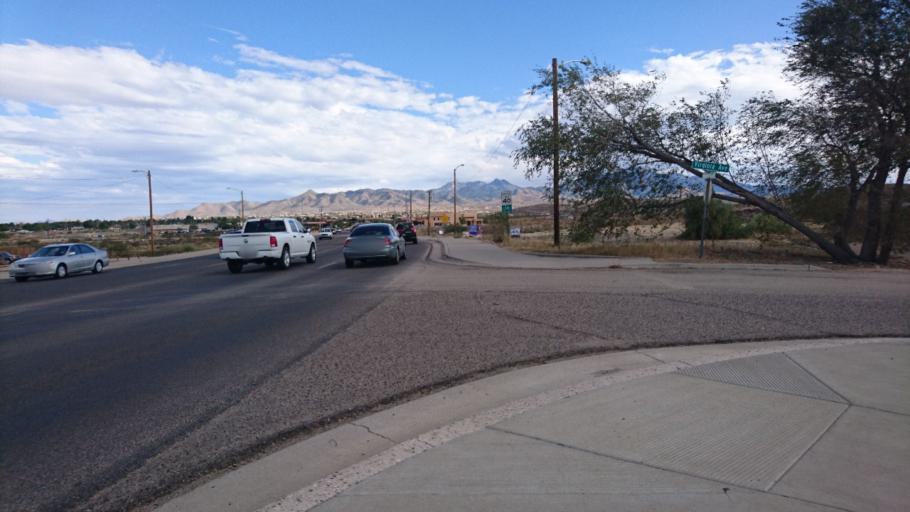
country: US
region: Arizona
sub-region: Mohave County
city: Kingman
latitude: 35.1942
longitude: -114.0317
